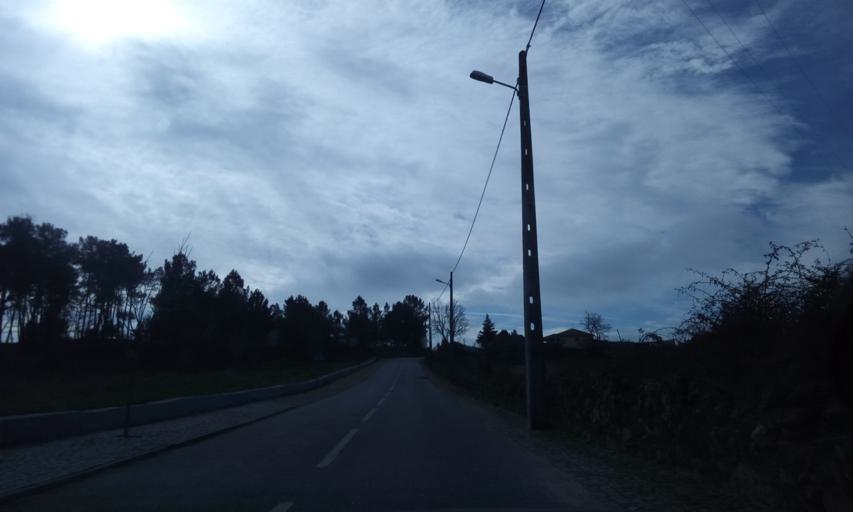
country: PT
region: Guarda
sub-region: Fornos de Algodres
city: Fornos de Algodres
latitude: 40.6769
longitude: -7.5300
